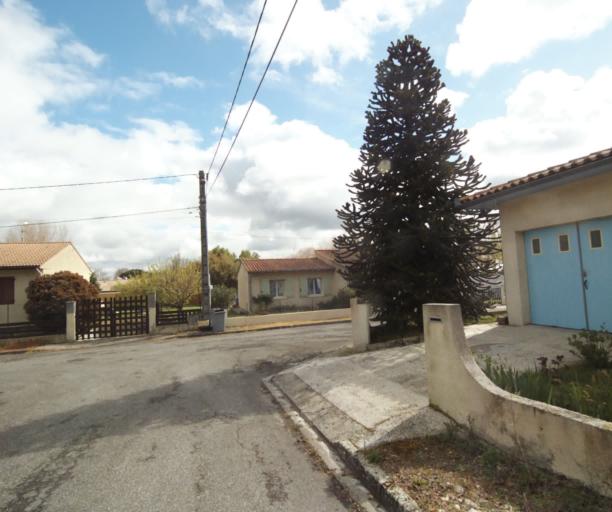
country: FR
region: Midi-Pyrenees
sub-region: Departement de l'Ariege
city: Saverdun
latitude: 43.2371
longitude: 1.5705
